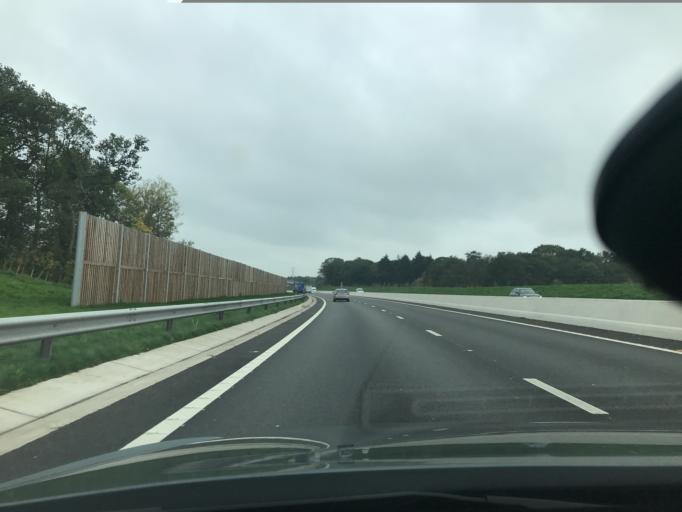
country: GB
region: England
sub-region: Cheshire East
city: Mere
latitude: 53.3294
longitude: -2.4224
